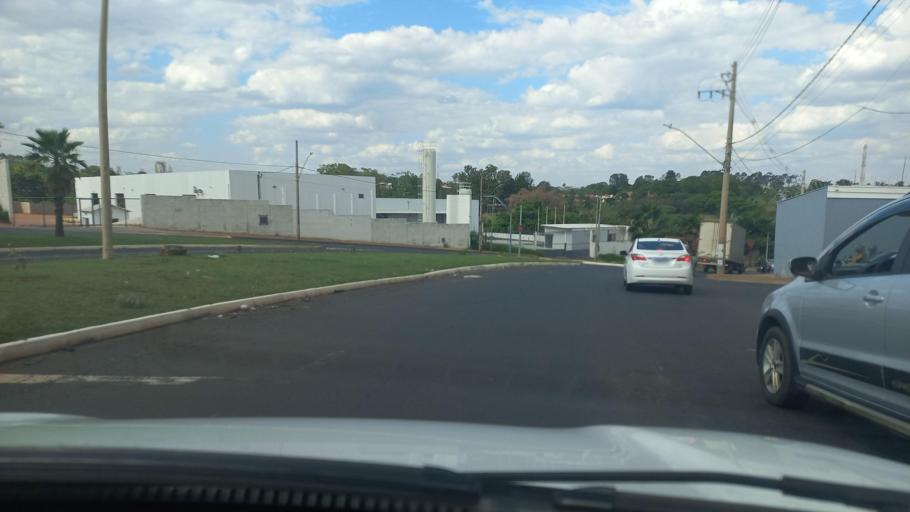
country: BR
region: Minas Gerais
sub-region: Uberaba
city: Uberaba
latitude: -19.7517
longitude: -47.9852
